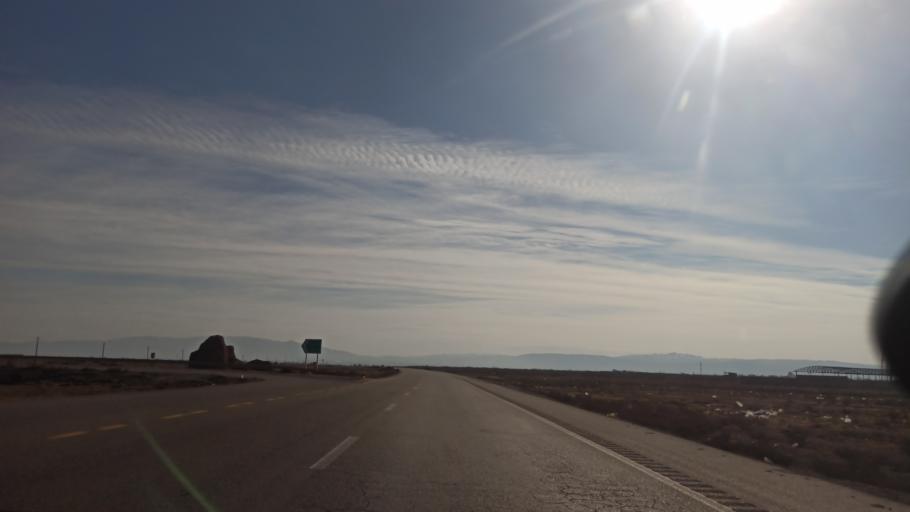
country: IR
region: Qazvin
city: Bu'in Zahra
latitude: 35.8141
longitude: 50.0756
